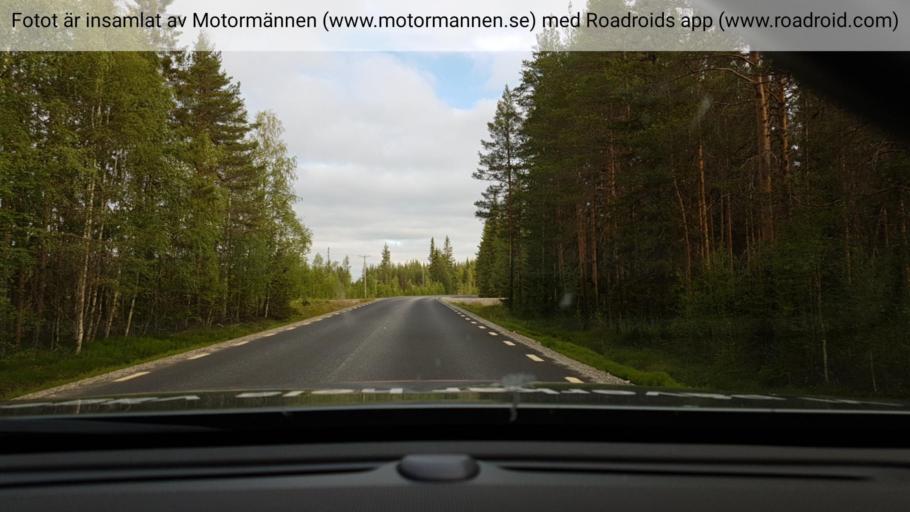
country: SE
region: Vaesterbotten
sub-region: Norsjo Kommun
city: Norsjoe
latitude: 64.4736
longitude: 19.3250
